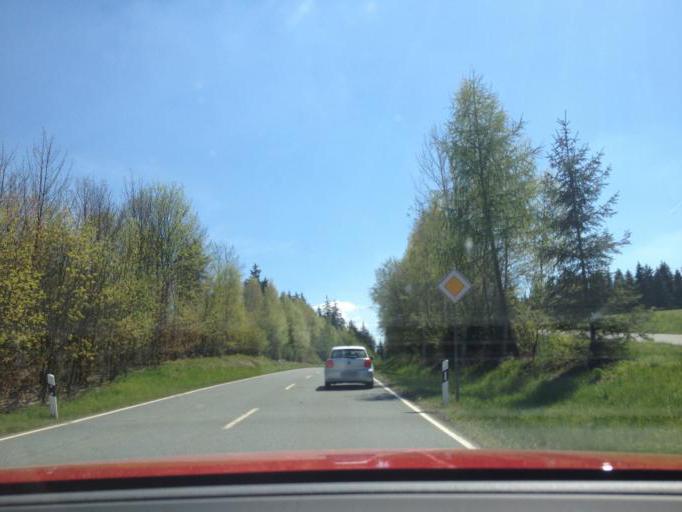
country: DE
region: Bavaria
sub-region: Upper Franconia
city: Schwarzenbach an der Saale
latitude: 50.2020
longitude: 11.9425
